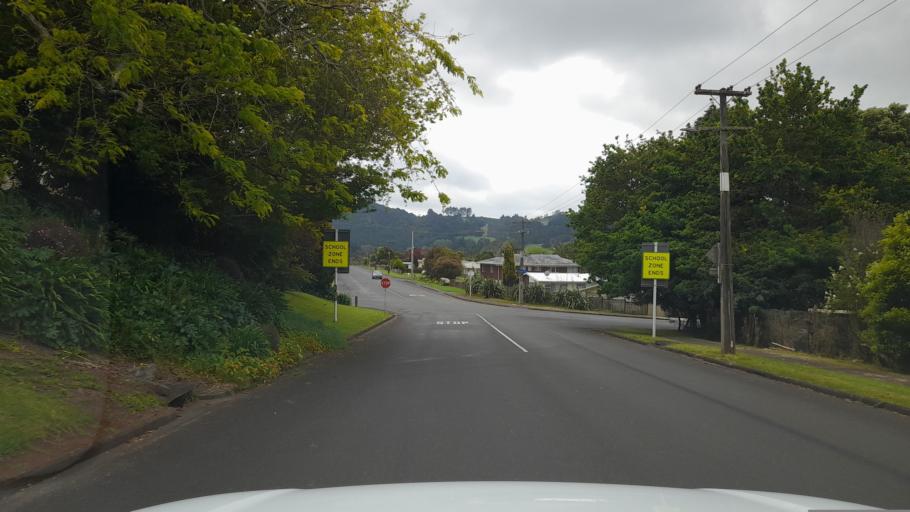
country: NZ
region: Northland
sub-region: Far North District
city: Waimate North
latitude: -35.4066
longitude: 173.7901
